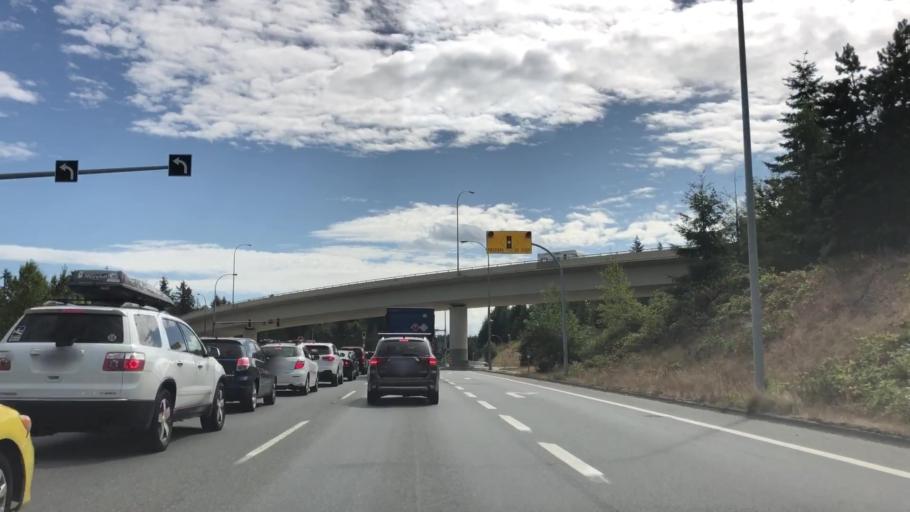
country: CA
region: British Columbia
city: Nanaimo
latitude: 49.1256
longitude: -123.9177
